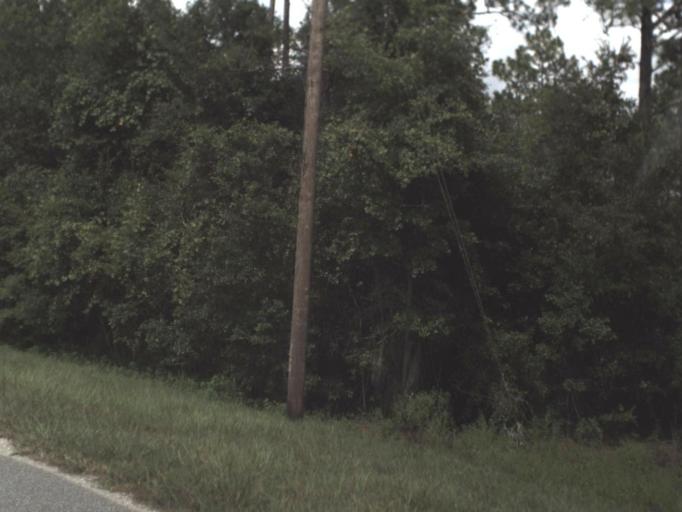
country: US
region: Florida
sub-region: Citrus County
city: Floral City
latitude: 28.6607
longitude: -82.3230
